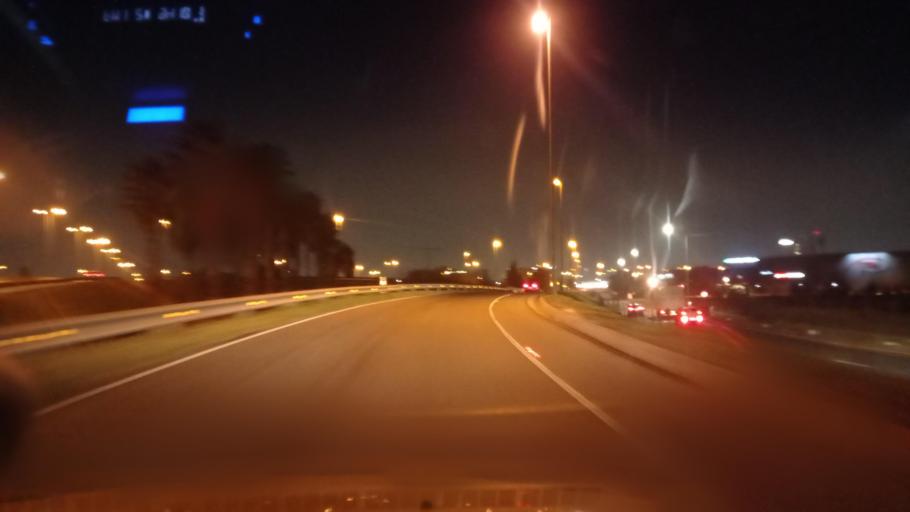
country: CL
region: Santiago Metropolitan
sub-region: Provincia de Santiago
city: Lo Prado
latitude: -33.4228
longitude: -70.7854
